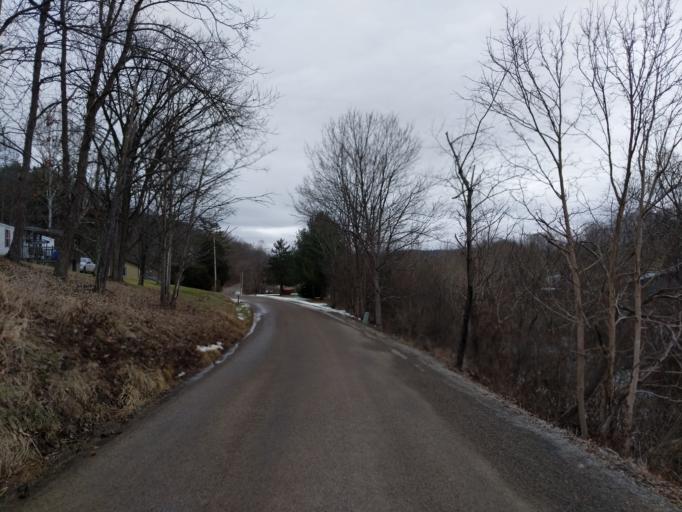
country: US
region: Ohio
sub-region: Athens County
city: The Plains
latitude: 39.3341
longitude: -82.1463
